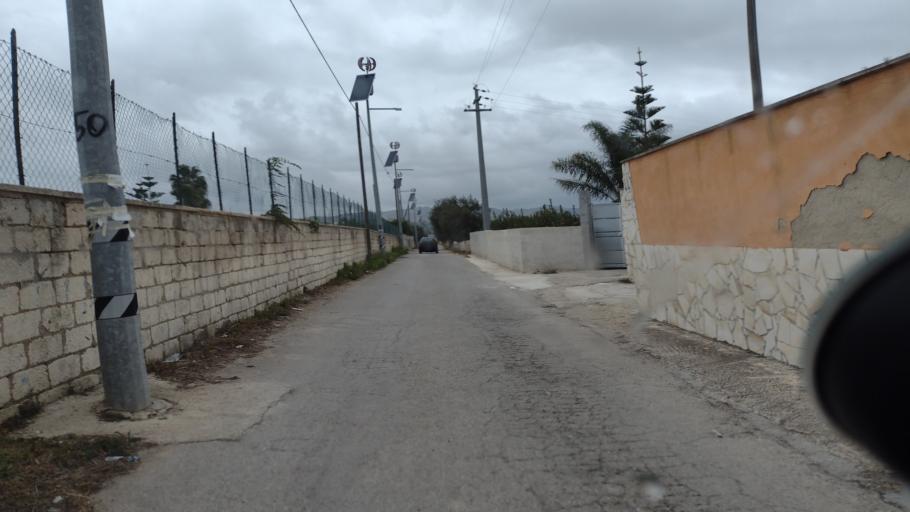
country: IT
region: Sicily
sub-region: Provincia di Siracusa
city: Avola
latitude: 36.8878
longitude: 15.1211
